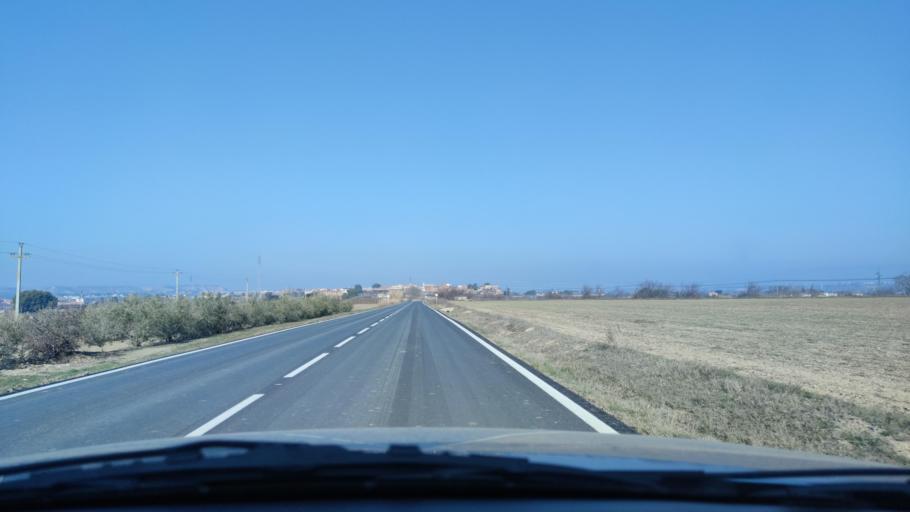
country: ES
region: Catalonia
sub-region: Provincia de Lleida
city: Torrefarrera
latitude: 41.7012
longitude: 0.6269
